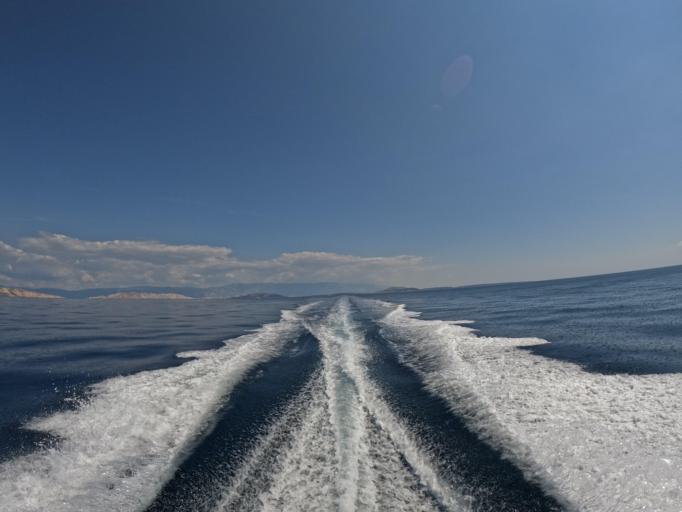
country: HR
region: Primorsko-Goranska
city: Punat
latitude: 44.9081
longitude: 14.5970
